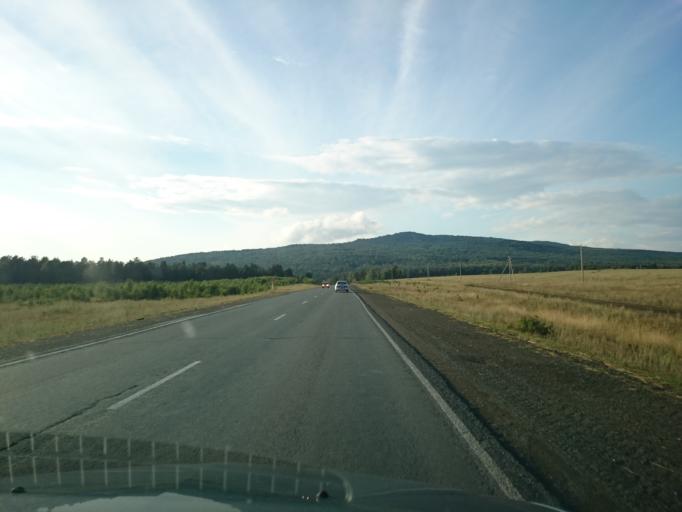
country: RU
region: Bashkortostan
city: Lomovka
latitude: 53.8901
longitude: 58.0957
